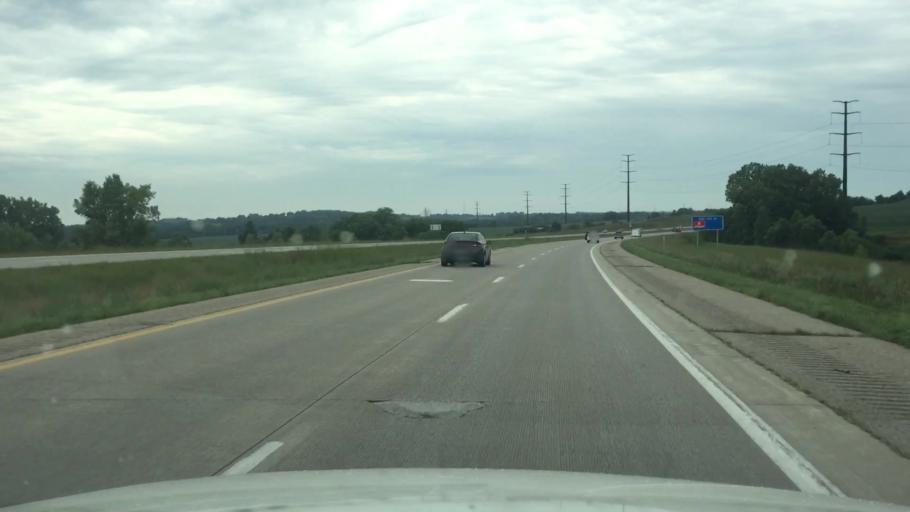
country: US
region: Iowa
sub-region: Warren County
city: Norwalk
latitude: 41.4980
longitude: -93.6030
